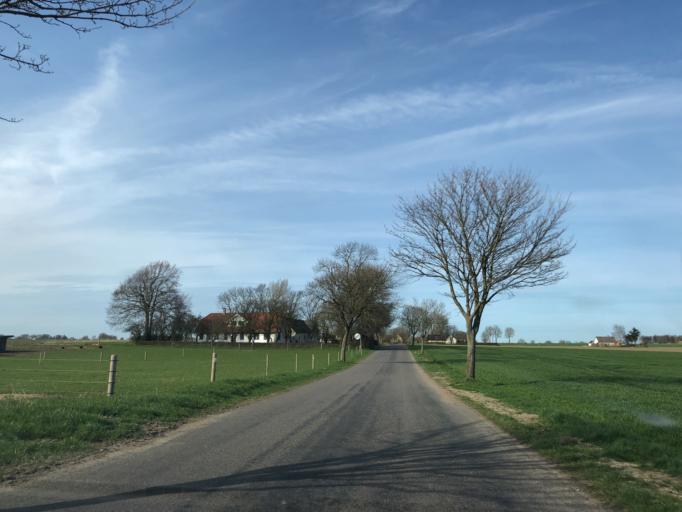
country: DK
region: Zealand
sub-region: Stevns Kommune
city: Store Heddinge
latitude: 55.2854
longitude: 12.4428
